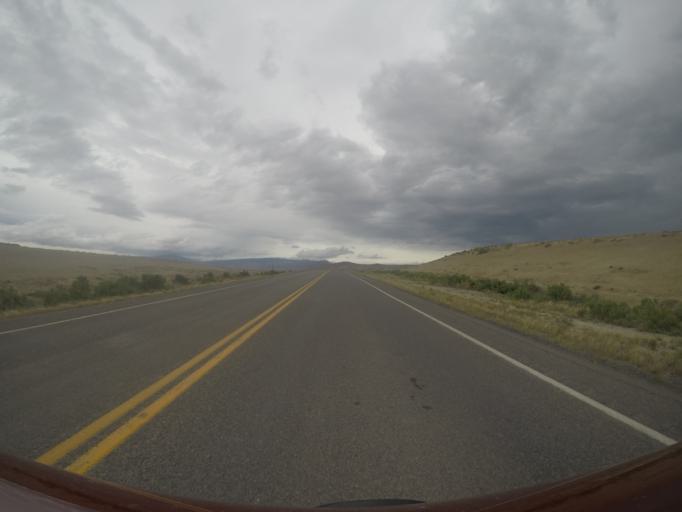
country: US
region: Wyoming
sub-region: Big Horn County
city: Lovell
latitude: 44.8881
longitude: -108.2889
